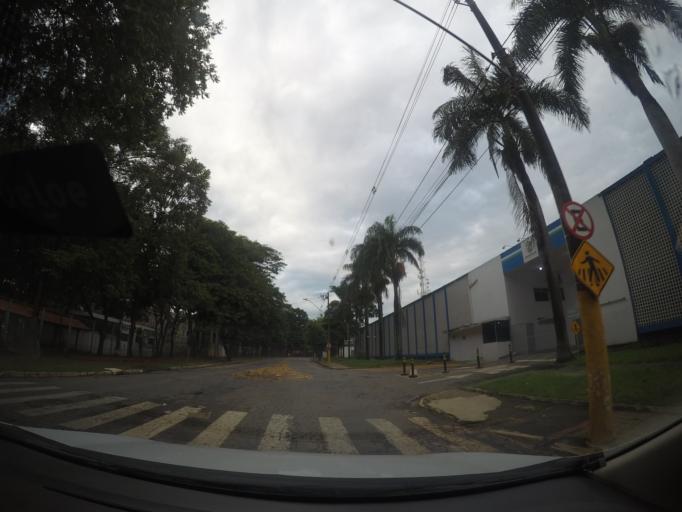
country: BR
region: Goias
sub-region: Goiania
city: Goiania
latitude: -16.6637
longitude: -49.2540
